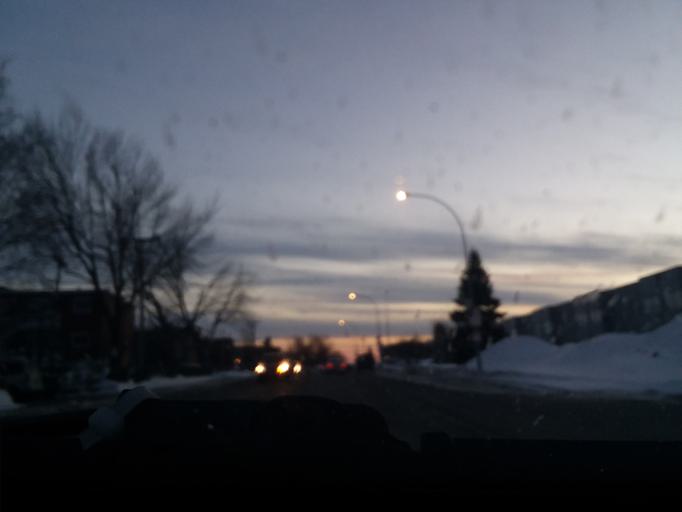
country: CA
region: Quebec
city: Montreal-Ouest
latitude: 45.4426
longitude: -73.6290
